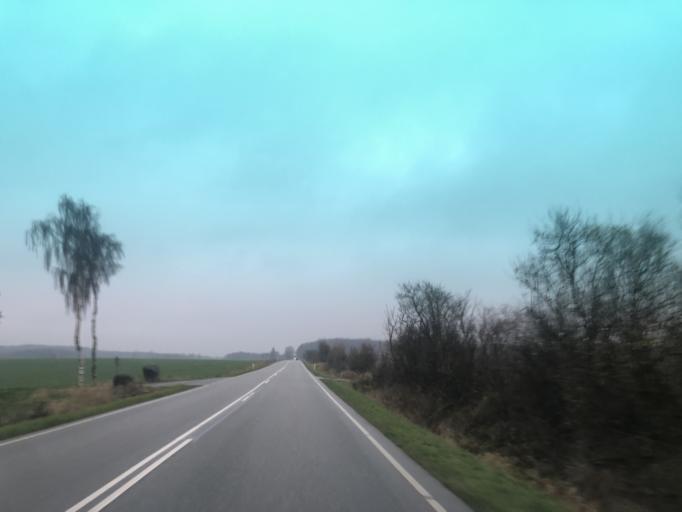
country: DK
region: South Denmark
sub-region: Nyborg Kommune
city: Ullerslev
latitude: 55.2475
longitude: 10.6634
